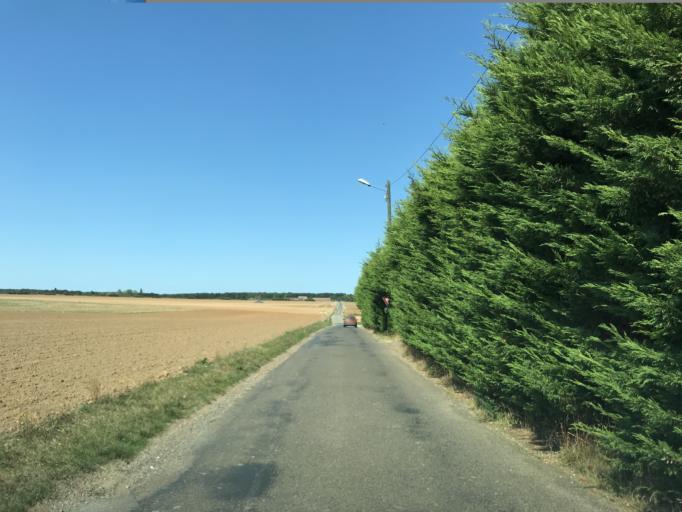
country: FR
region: Haute-Normandie
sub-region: Departement de l'Eure
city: Houlbec-Cocherel
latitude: 49.0641
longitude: 1.2690
